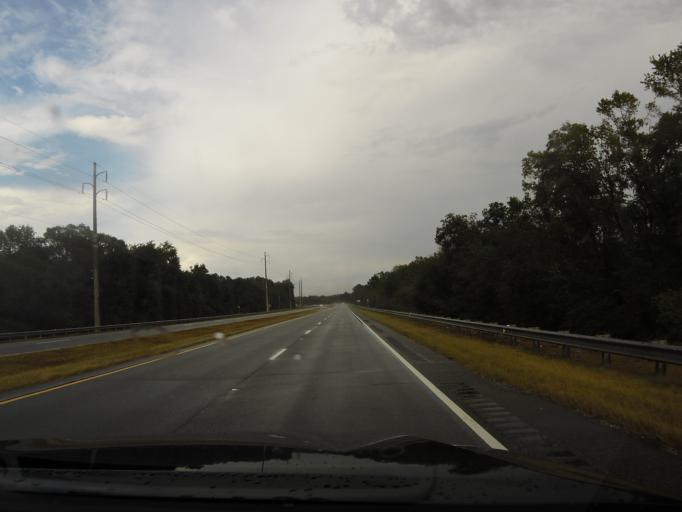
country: US
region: Georgia
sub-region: Long County
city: Ludowici
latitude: 31.6800
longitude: -81.8106
